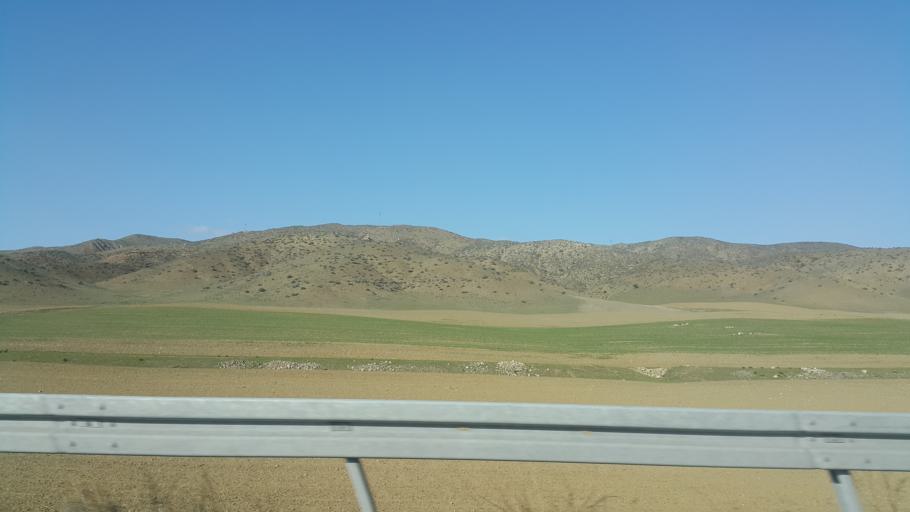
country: TR
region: Ankara
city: Sereflikochisar
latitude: 38.8111
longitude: 33.6078
